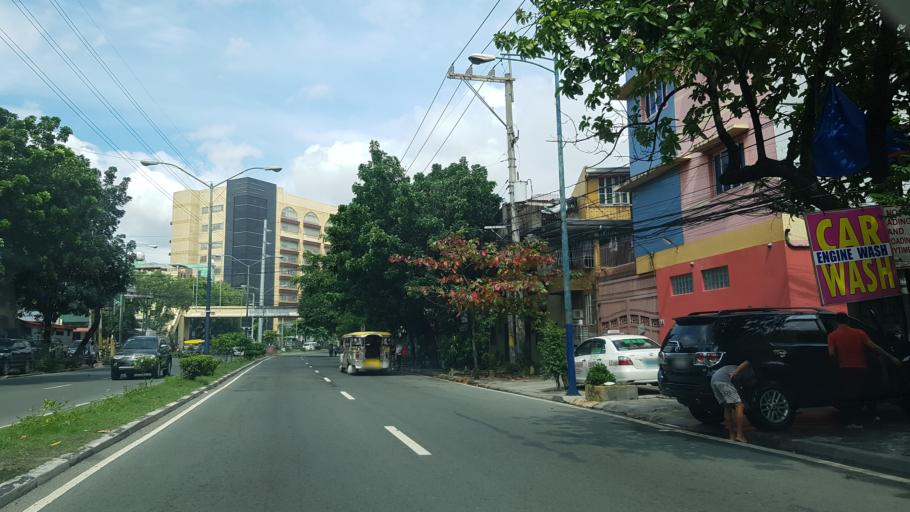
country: PH
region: Metro Manila
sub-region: Makati City
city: Makati City
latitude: 14.5620
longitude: 121.0505
